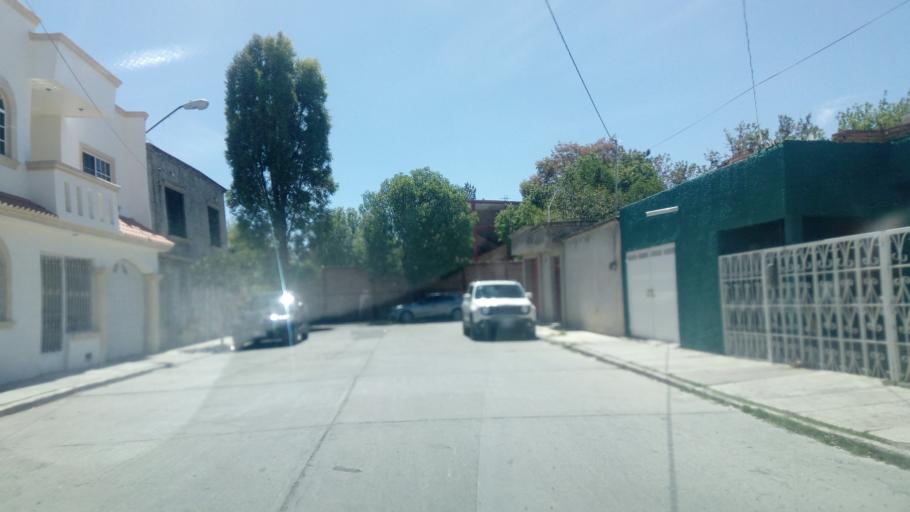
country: MX
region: Durango
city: Victoria de Durango
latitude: 24.0106
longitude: -104.6596
